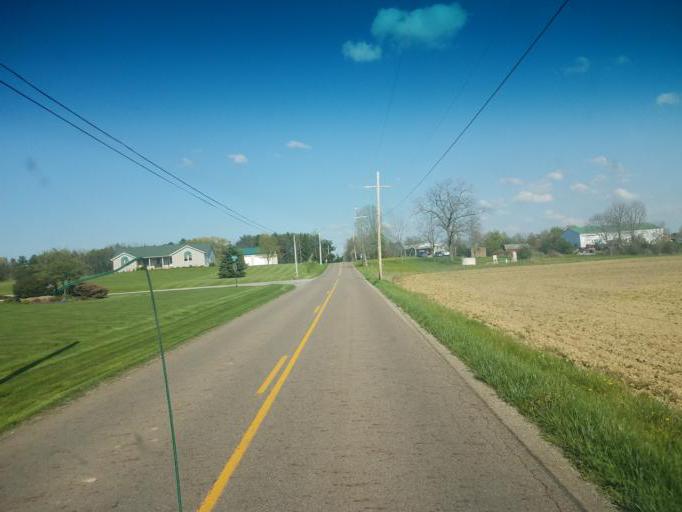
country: US
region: Ohio
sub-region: Wayne County
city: Smithville
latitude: 40.8796
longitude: -81.9154
